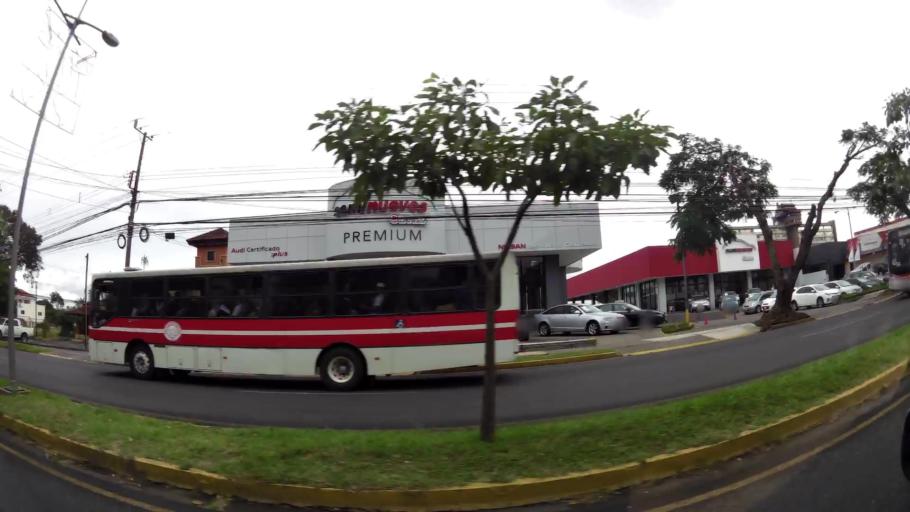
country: CR
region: San Jose
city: San Jose
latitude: 9.9380
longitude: -84.1007
